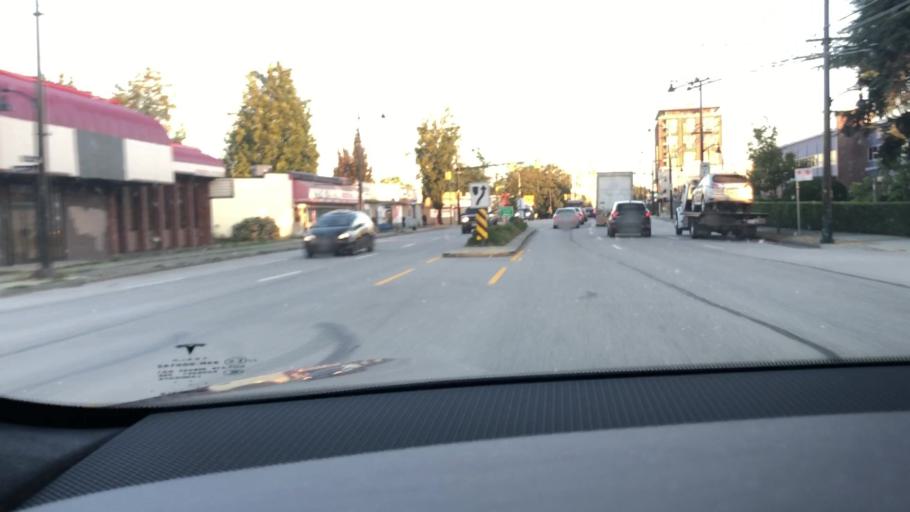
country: CA
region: British Columbia
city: Vancouver
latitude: 49.2371
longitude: -123.0475
